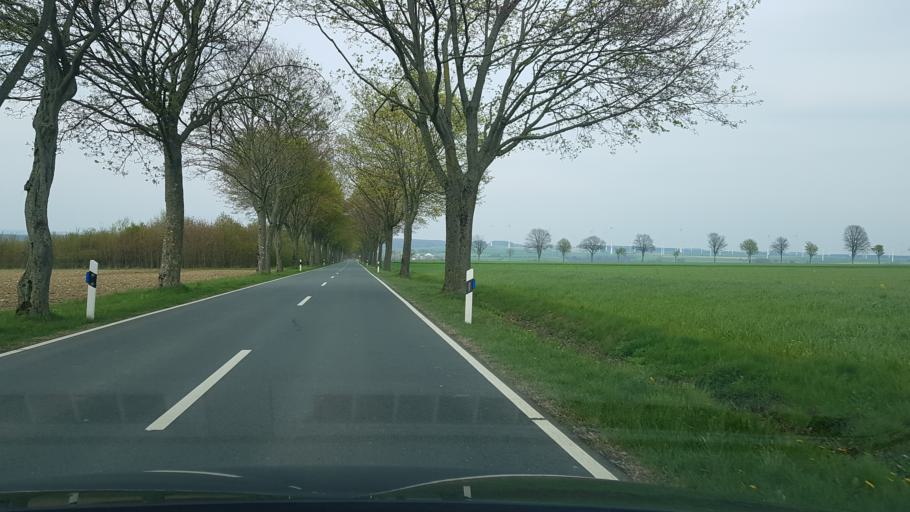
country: DE
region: North Rhine-Westphalia
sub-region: Regierungsbezirk Detmold
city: Wunnenberg
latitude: 51.6160
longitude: 8.7361
